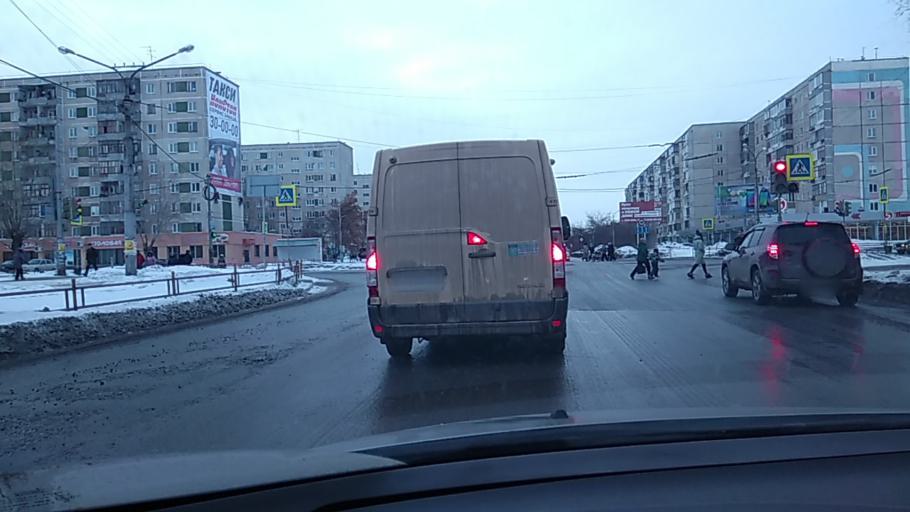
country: RU
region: Sverdlovsk
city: Martyush
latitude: 56.4265
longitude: 61.8921
